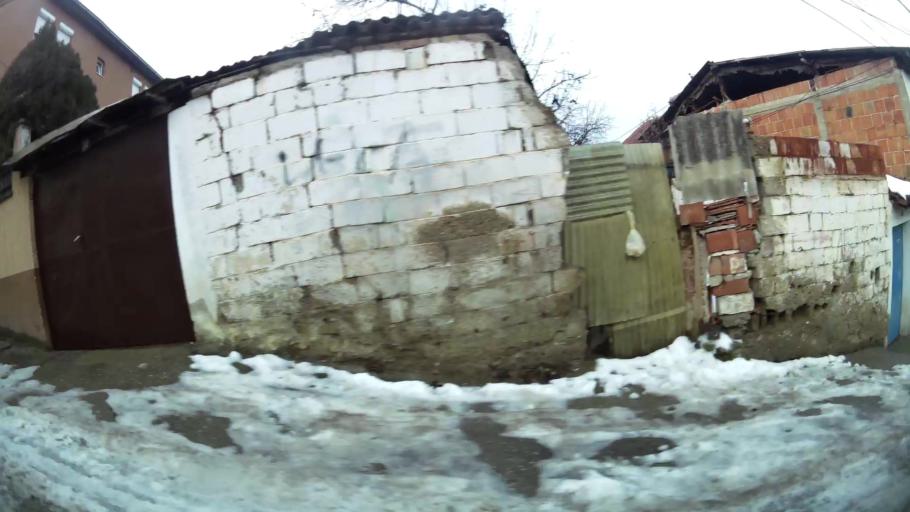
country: XK
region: Pristina
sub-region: Komuna e Prishtines
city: Pristina
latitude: 42.6638
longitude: 21.1719
